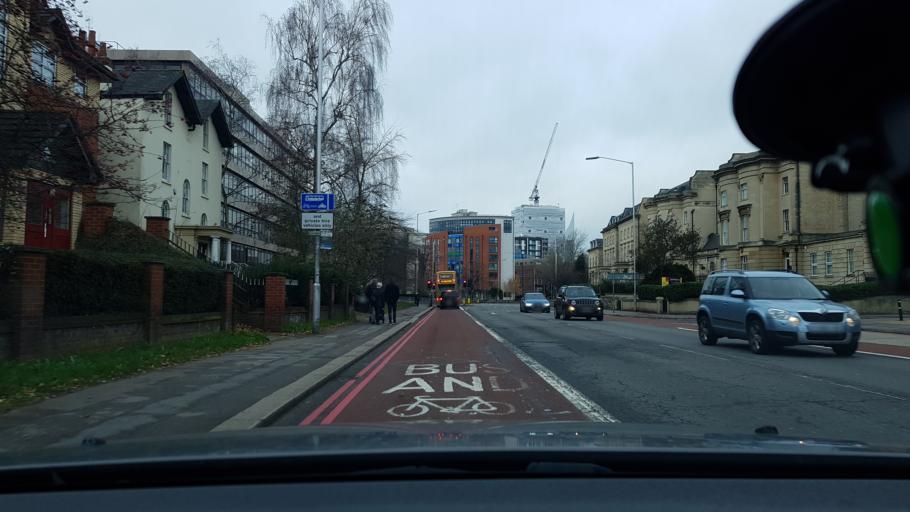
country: GB
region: England
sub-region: Reading
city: Reading
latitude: 51.4537
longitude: -0.9569
